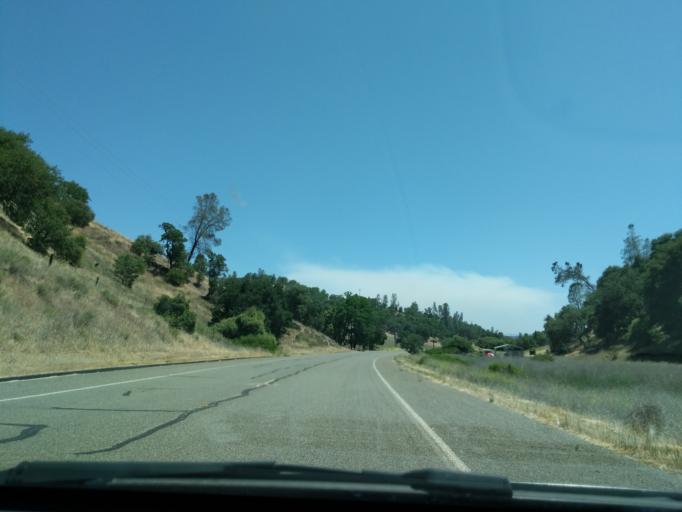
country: US
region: California
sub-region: Monterey County
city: King City
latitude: 36.0541
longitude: -121.1819
